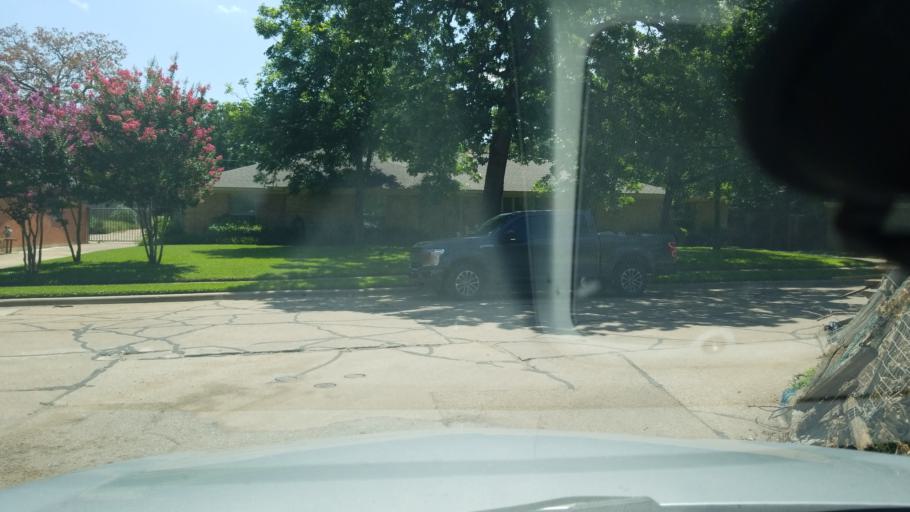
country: US
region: Texas
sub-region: Dallas County
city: Irving
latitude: 32.8305
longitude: -96.9534
